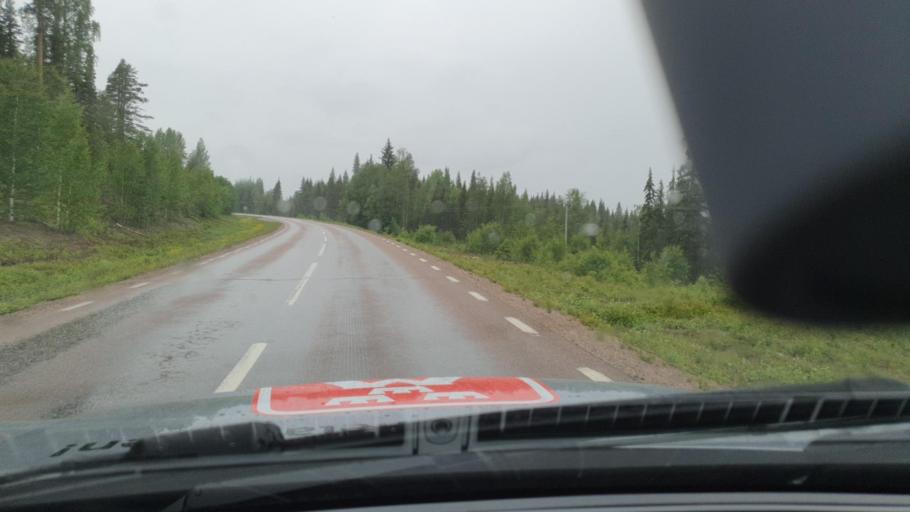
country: SE
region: Norrbotten
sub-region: Overtornea Kommun
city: OEvertornea
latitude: 66.4486
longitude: 23.3037
